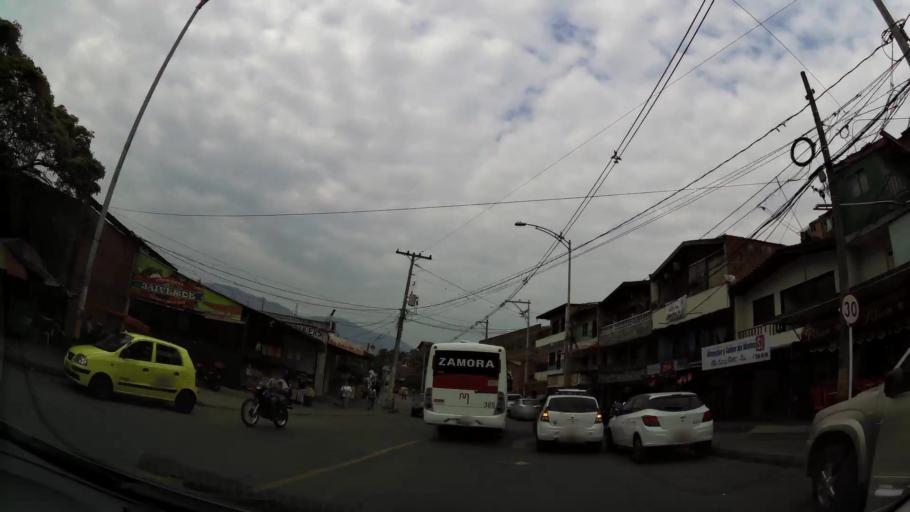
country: CO
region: Antioquia
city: Bello
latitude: 6.3007
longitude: -75.5568
